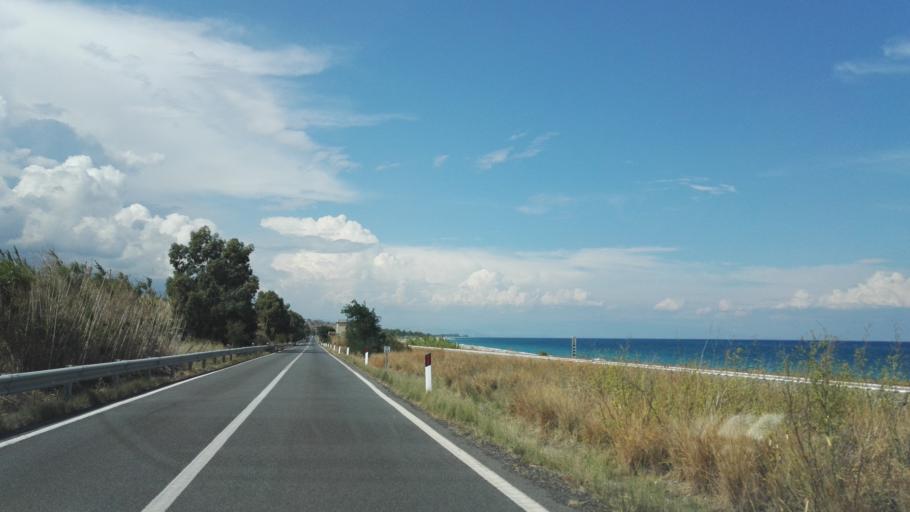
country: IT
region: Calabria
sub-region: Provincia di Catanzaro
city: Santa Caterina dello Ionio Marina
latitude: 38.5056
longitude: 16.5759
